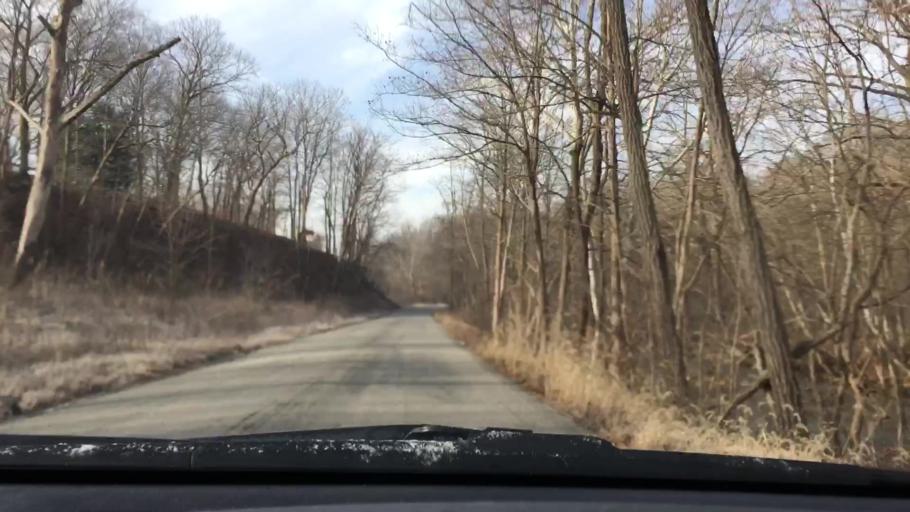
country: US
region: Pennsylvania
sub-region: Westmoreland County
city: Collinsburg
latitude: 40.2616
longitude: -79.7242
